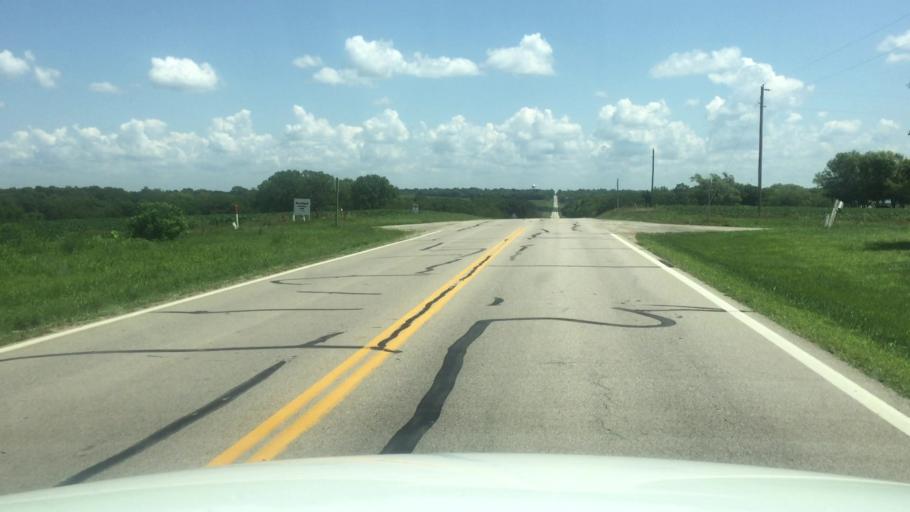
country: US
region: Kansas
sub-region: Brown County
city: Horton
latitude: 39.6674
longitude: -95.5646
